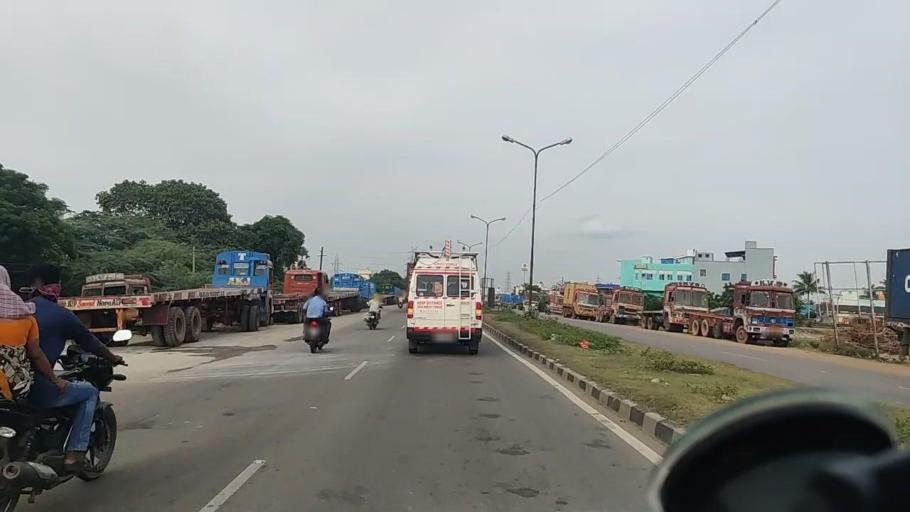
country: IN
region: Tamil Nadu
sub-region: Thiruvallur
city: Chinnasekkadu
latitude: 13.1779
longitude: 80.2484
